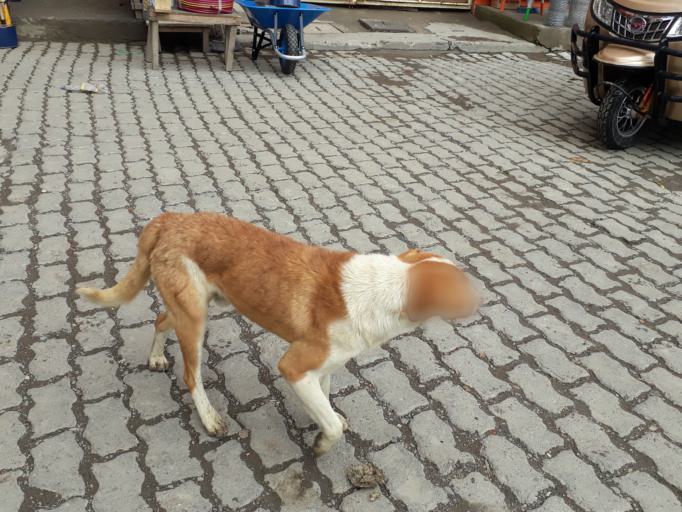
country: BO
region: La Paz
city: Achacachi
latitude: -16.0451
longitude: -68.6853
